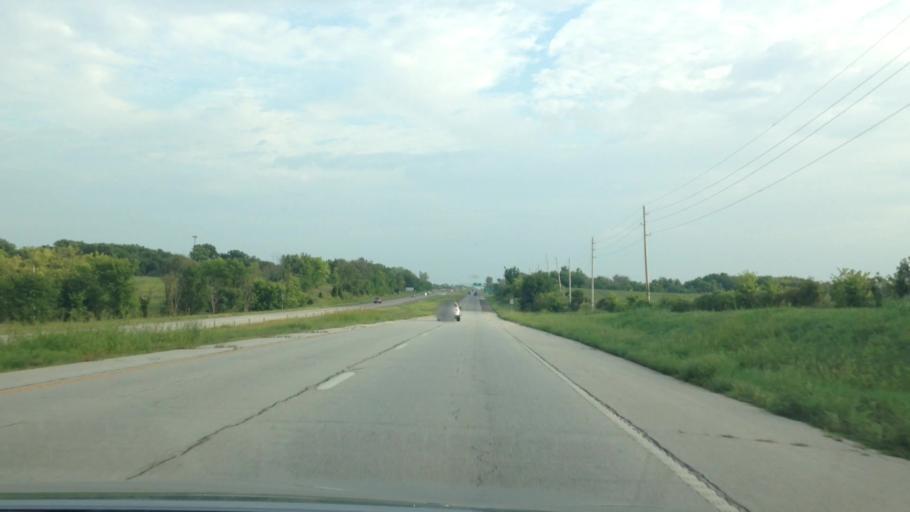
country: US
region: Missouri
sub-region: Clay County
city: Smithville
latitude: 39.3237
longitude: -94.5845
